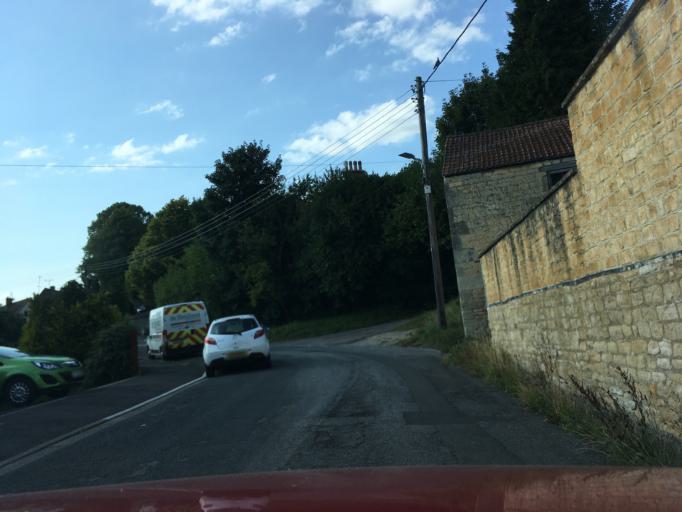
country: GB
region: England
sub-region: Gloucestershire
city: Stroud
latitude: 51.7364
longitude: -2.2278
